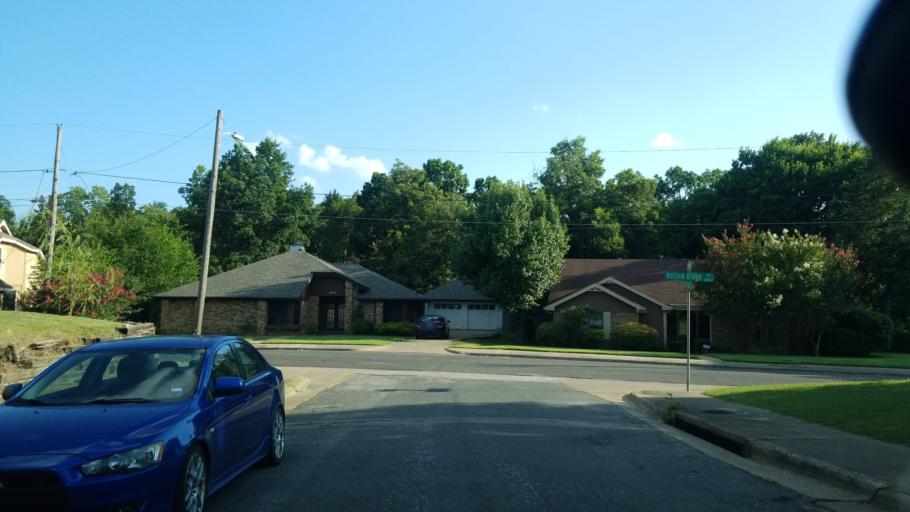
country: US
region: Texas
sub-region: Dallas County
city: Dallas
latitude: 32.7813
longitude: -96.7096
